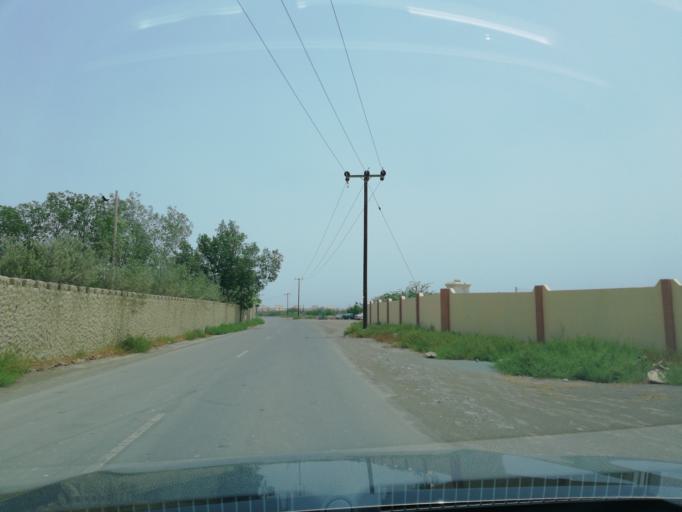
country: OM
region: Al Batinah
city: Al Liwa'
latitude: 24.6094
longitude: 56.5381
